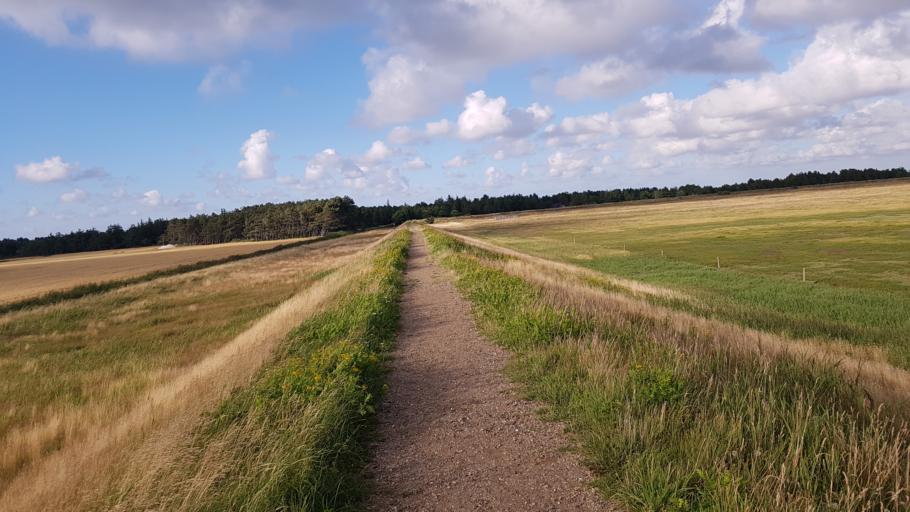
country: DE
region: Schleswig-Holstein
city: List
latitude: 55.0799
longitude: 8.5290
